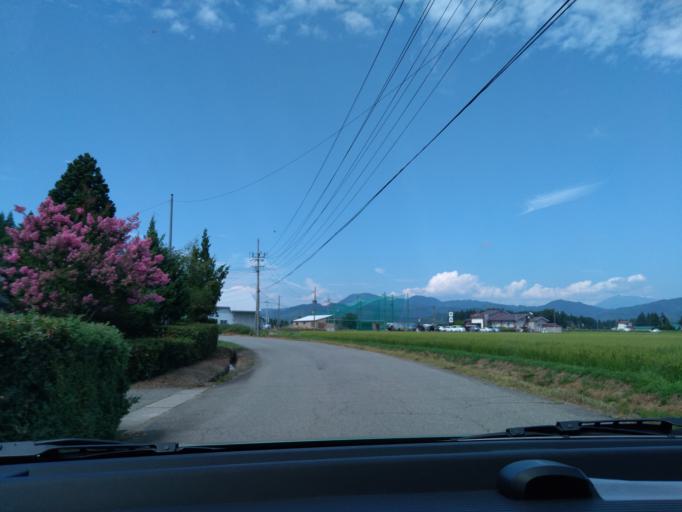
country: JP
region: Akita
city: Kakunodatemachi
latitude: 39.6116
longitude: 140.5946
